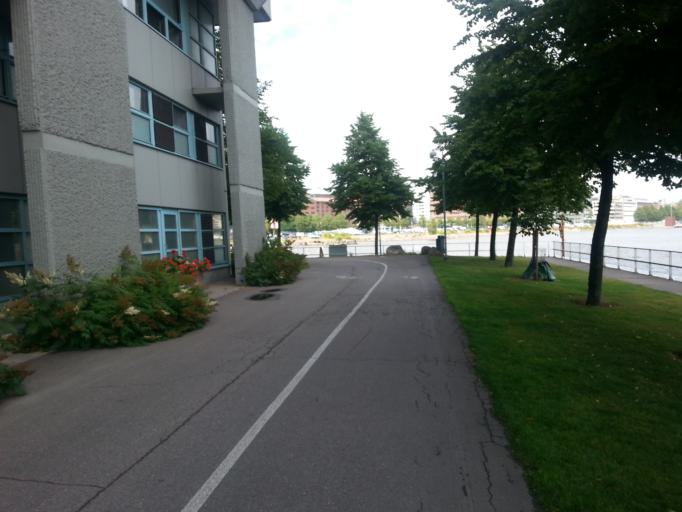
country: FI
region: Uusimaa
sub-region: Helsinki
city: Helsinki
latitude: 60.1801
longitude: 24.9633
